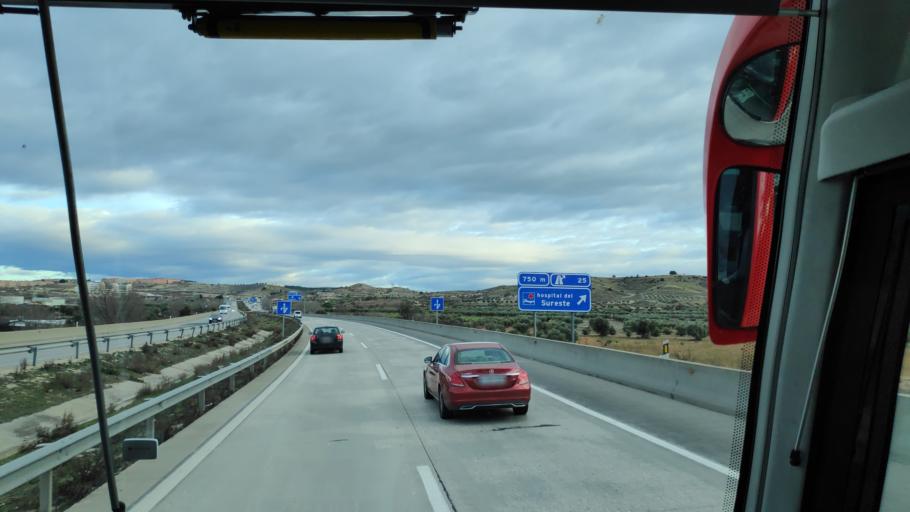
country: ES
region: Madrid
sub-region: Provincia de Madrid
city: Vaciamadrid
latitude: 40.2986
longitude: -3.4808
